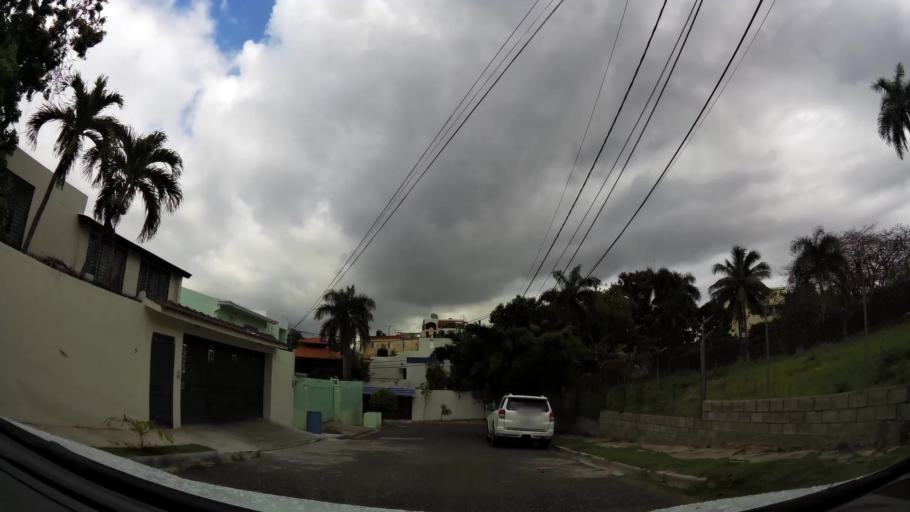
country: DO
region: Nacional
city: La Agustina
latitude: 18.4954
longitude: -69.9343
